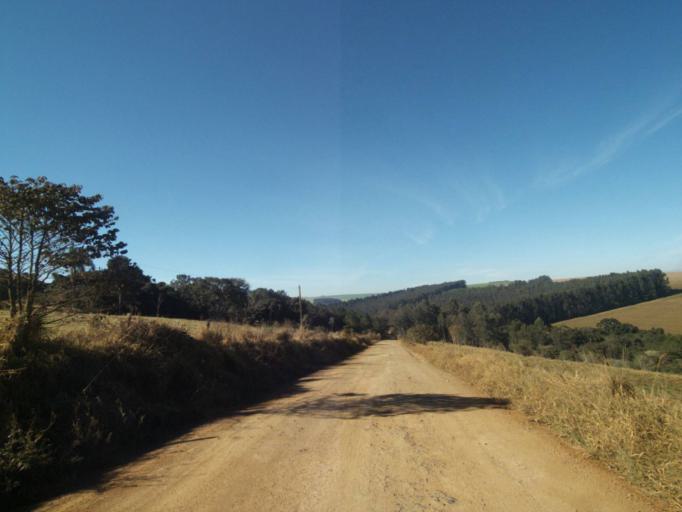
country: BR
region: Parana
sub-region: Tibagi
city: Tibagi
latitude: -24.5288
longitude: -50.3792
